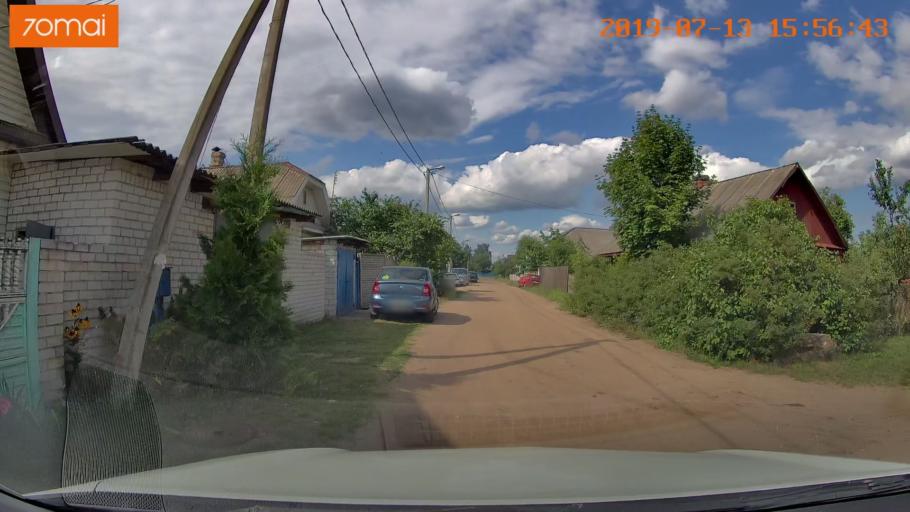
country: BY
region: Mogilev
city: Babruysk
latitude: 53.1445
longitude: 29.2022
